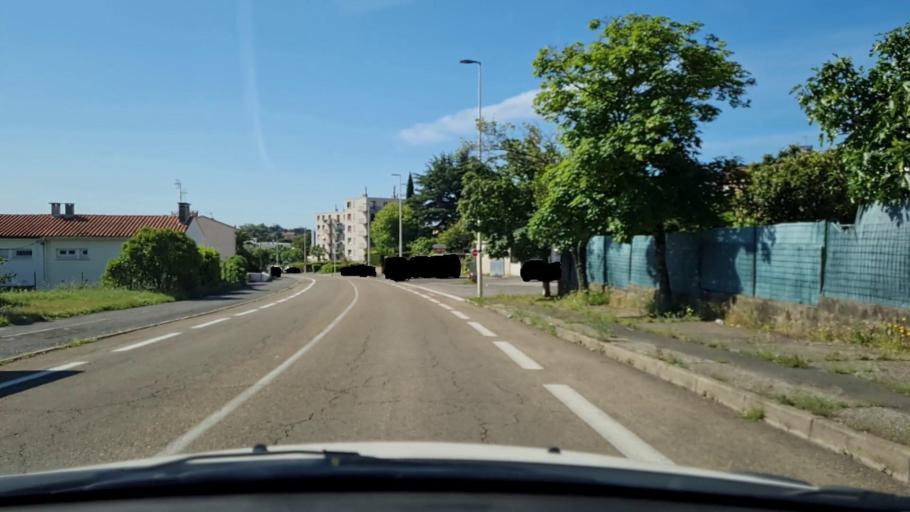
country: FR
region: Languedoc-Roussillon
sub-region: Departement du Gard
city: Ales
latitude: 44.1371
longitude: 4.0740
